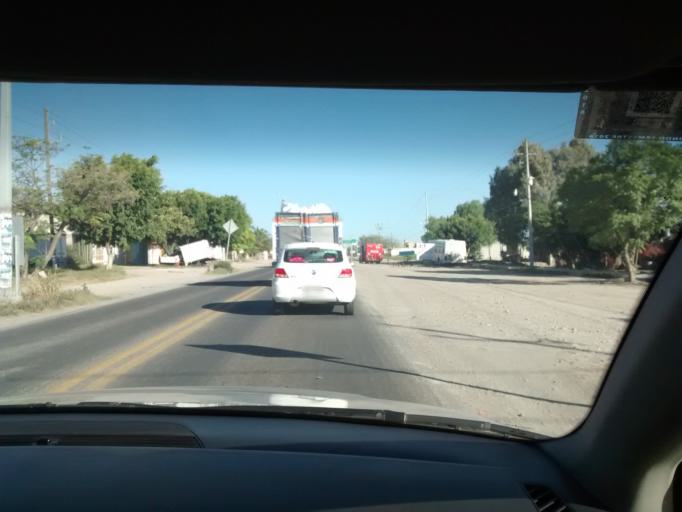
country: MX
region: Puebla
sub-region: Tehuacan
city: Magdalena Cuayucatepec
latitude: 18.5166
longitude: -97.5006
